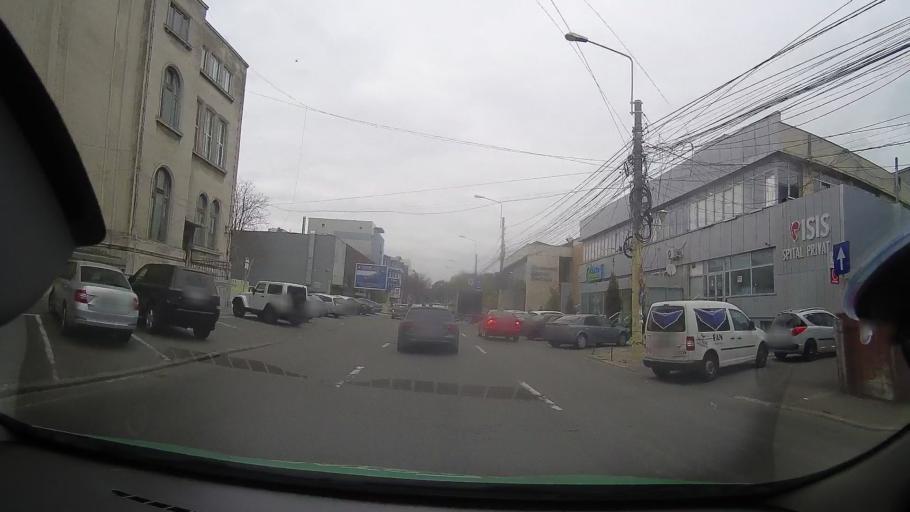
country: RO
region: Constanta
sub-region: Municipiul Constanta
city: Constanta
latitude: 44.1817
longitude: 28.6509
